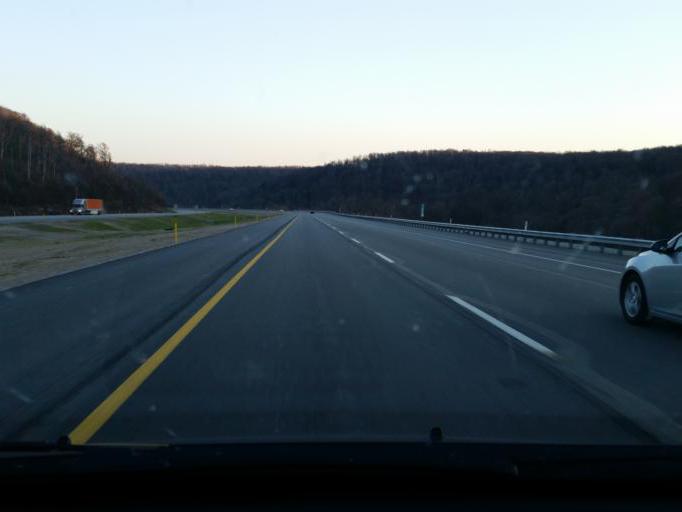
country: US
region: Pennsylvania
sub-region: Westmoreland County
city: Ligonier
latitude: 40.0968
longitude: -79.2025
